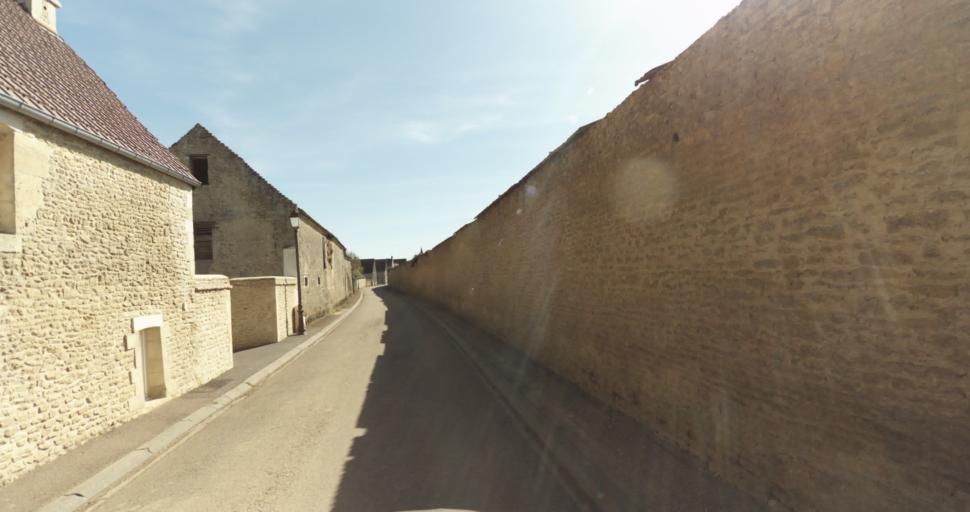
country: FR
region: Lower Normandy
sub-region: Departement du Calvados
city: Saint-Pierre-sur-Dives
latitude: 49.0402
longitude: -0.0262
